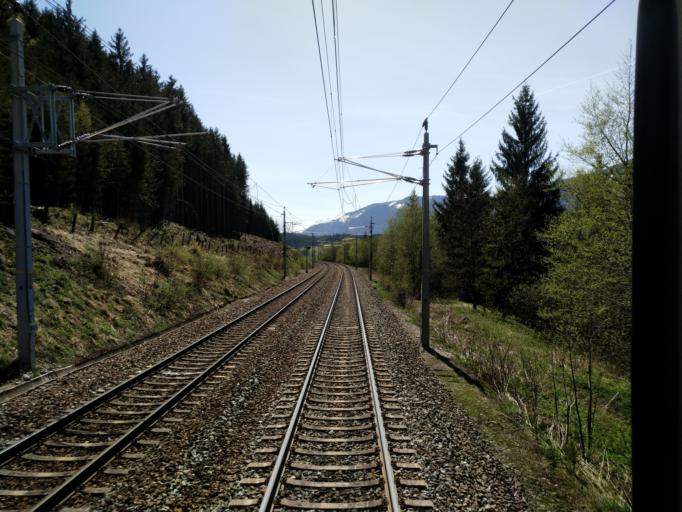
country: AT
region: Salzburg
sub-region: Politischer Bezirk Zell am See
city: Saalfelden am Steinernen Meer
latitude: 47.4153
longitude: 12.8287
